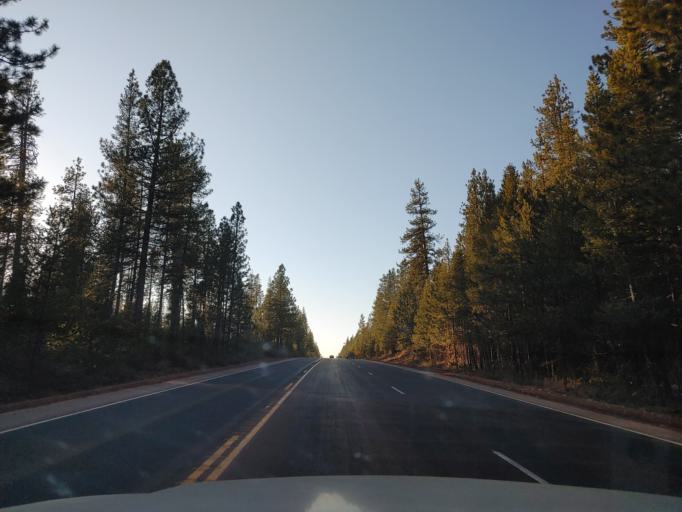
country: US
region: Oregon
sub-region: Deschutes County
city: La Pine
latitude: 43.4547
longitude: -121.8749
